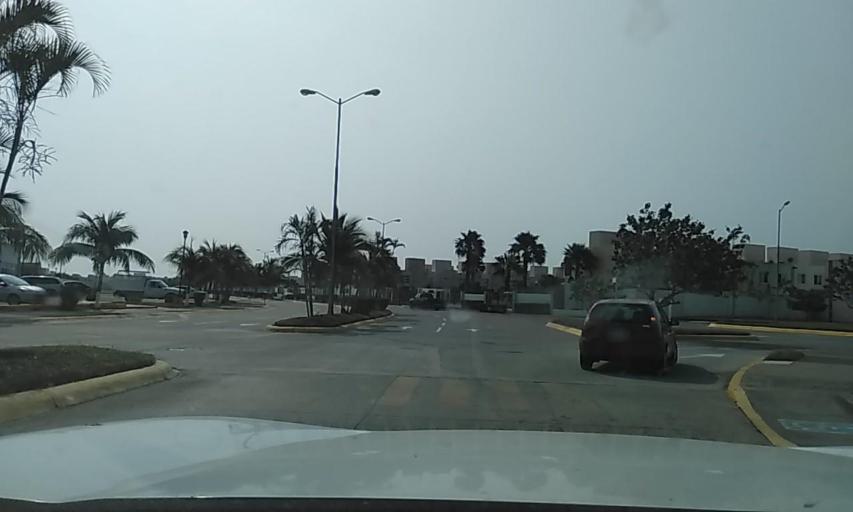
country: MX
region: Veracruz
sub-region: Veracruz
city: Hacienda Sotavento
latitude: 19.1304
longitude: -96.1715
